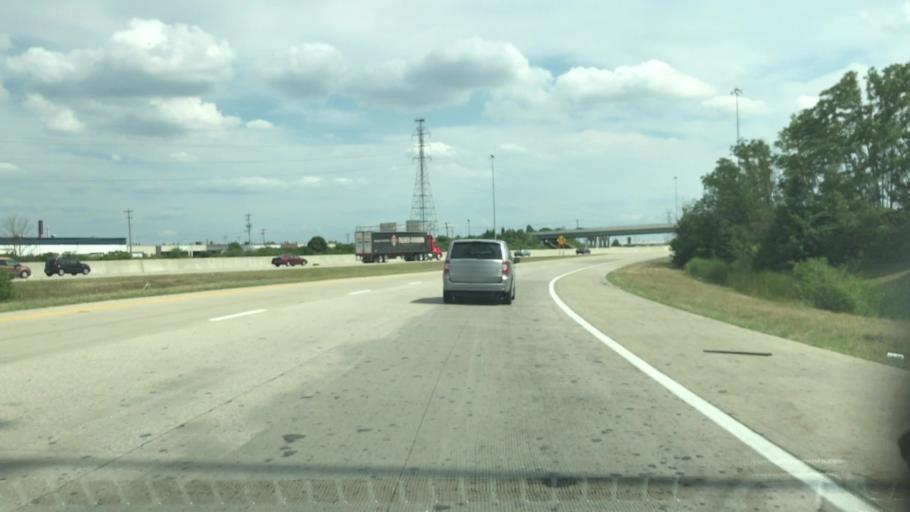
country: US
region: Ohio
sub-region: Franklin County
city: Lincoln Village
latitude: 39.9732
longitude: -83.1201
